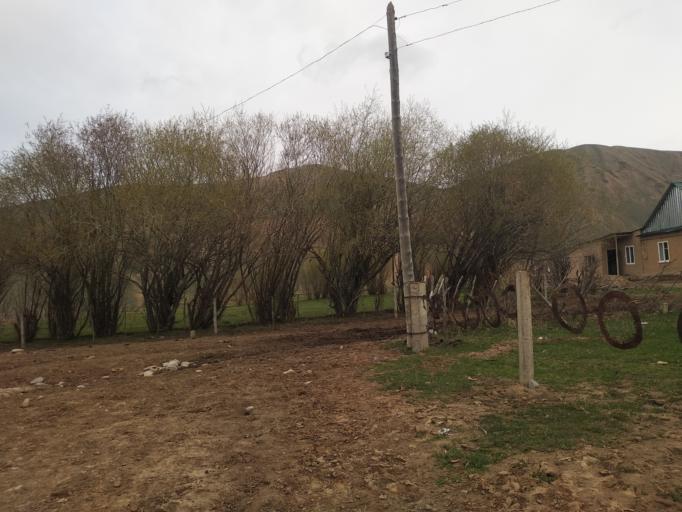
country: KG
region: Naryn
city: Naryn
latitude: 41.5211
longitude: 76.4361
